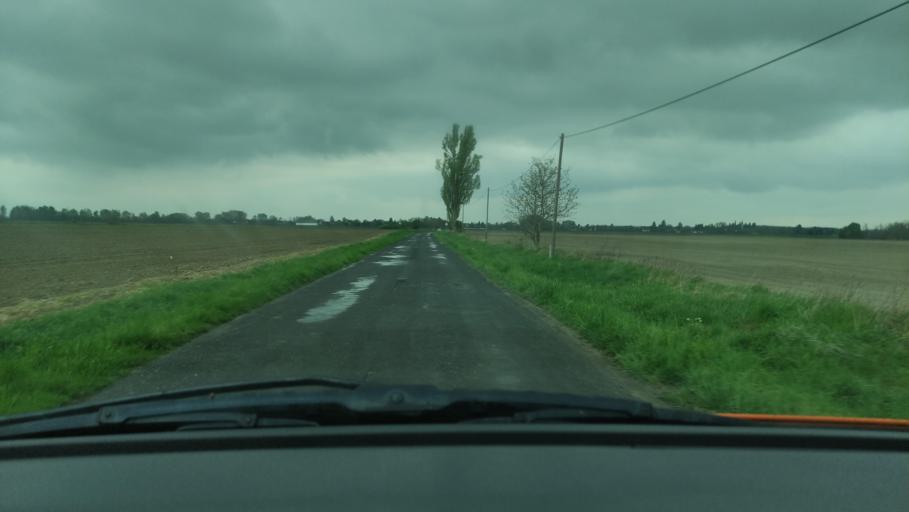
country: HU
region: Baranya
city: Mohacs
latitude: 45.9371
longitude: 18.7039
